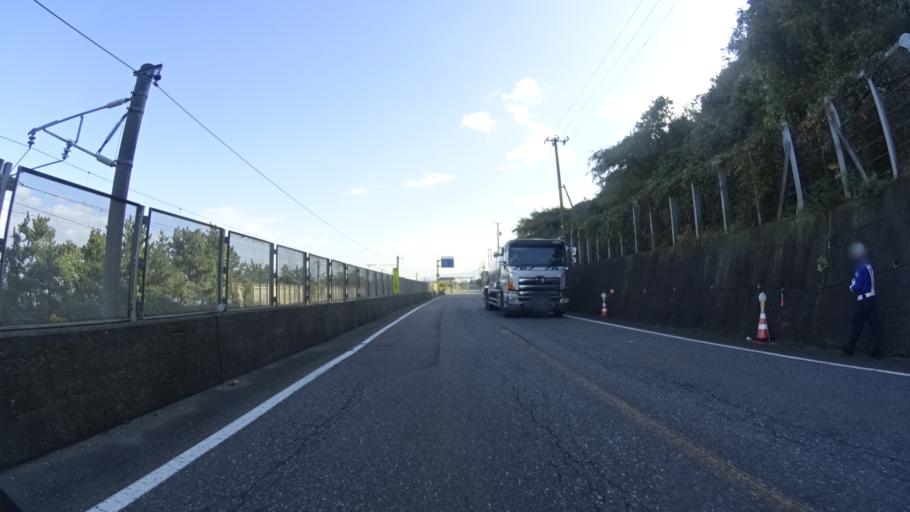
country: JP
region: Niigata
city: Itoigawa
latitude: 37.0214
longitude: 137.7835
